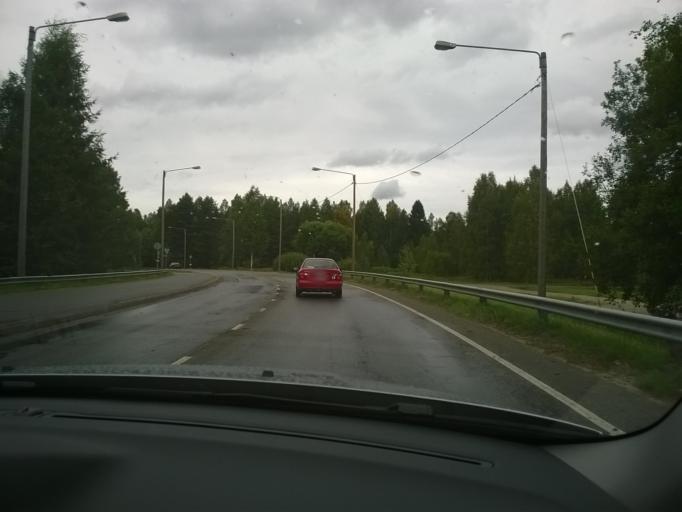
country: FI
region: Kainuu
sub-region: Kehys-Kainuu
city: Kuhmo
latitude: 64.1280
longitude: 29.5021
